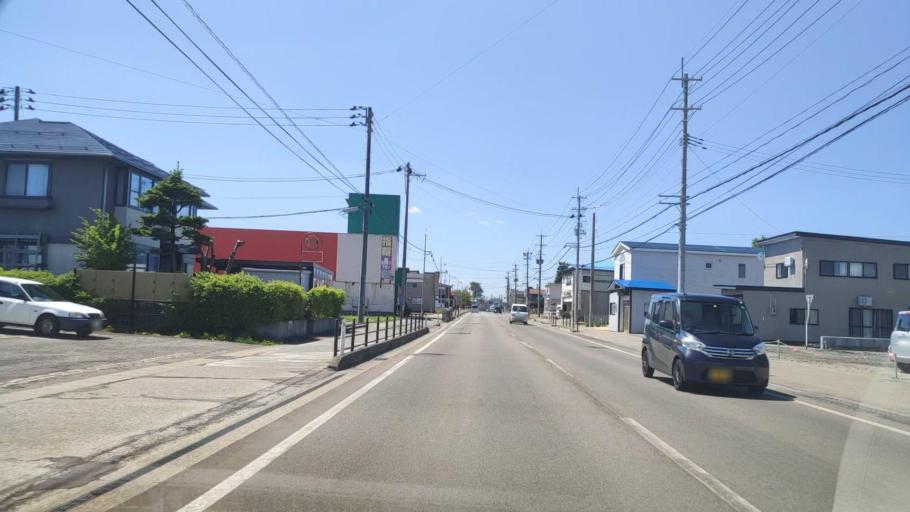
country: JP
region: Akita
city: Omagari
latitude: 39.4578
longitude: 140.4752
